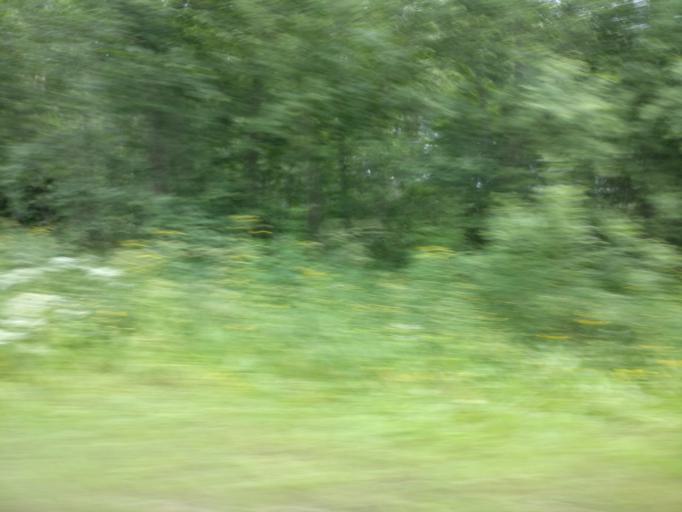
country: FI
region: Northern Savo
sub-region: Varkaus
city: Kangaslampi
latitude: 62.1724
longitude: 28.1107
